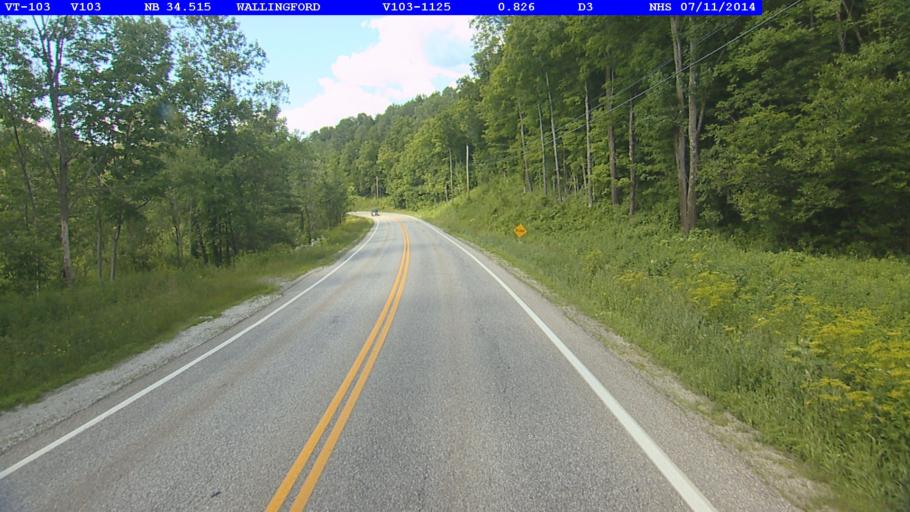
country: US
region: Vermont
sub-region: Rutland County
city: Rutland
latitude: 43.4619
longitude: -72.8731
